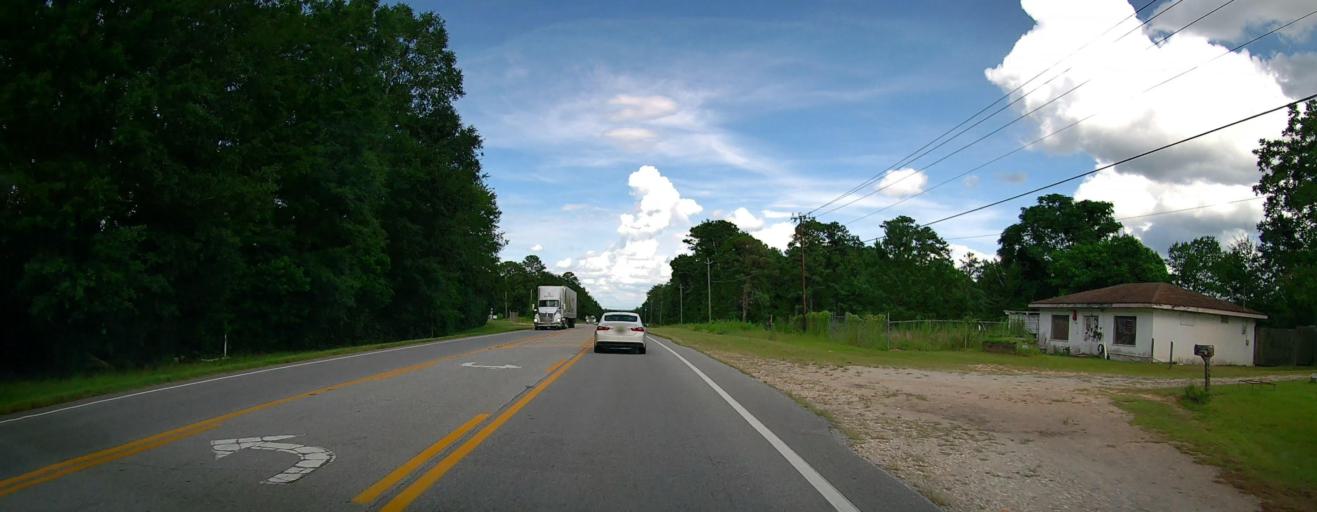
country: US
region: Alabama
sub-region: Russell County
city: Ladonia
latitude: 32.4571
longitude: -85.1855
